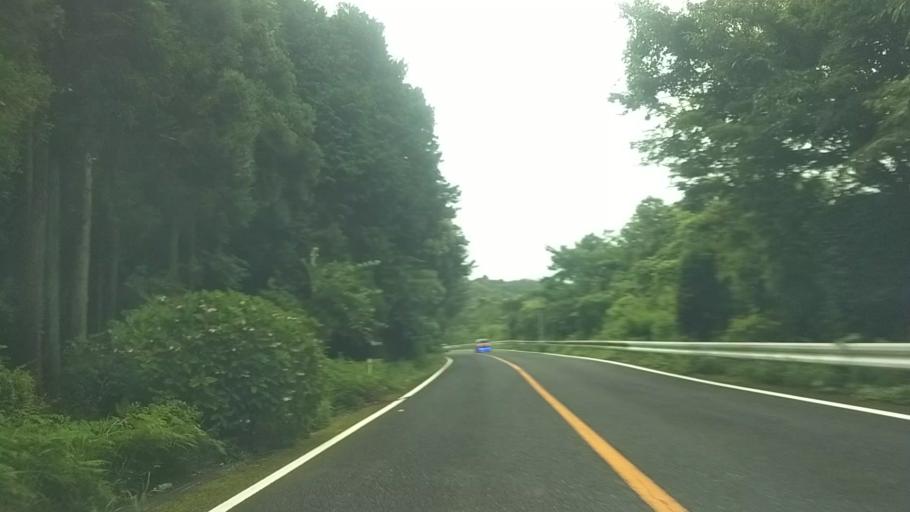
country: JP
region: Chiba
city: Kimitsu
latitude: 35.2335
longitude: 140.0154
